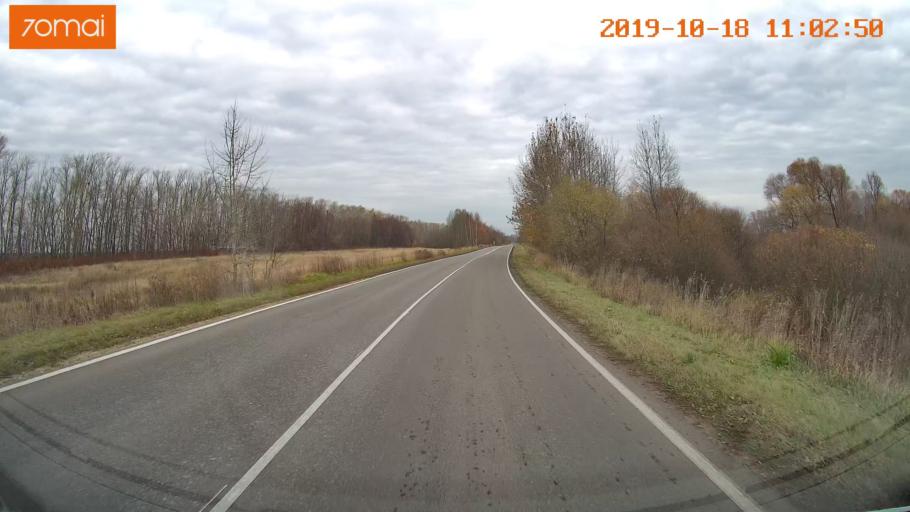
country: RU
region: Tula
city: Yepifan'
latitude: 53.8713
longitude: 38.5436
